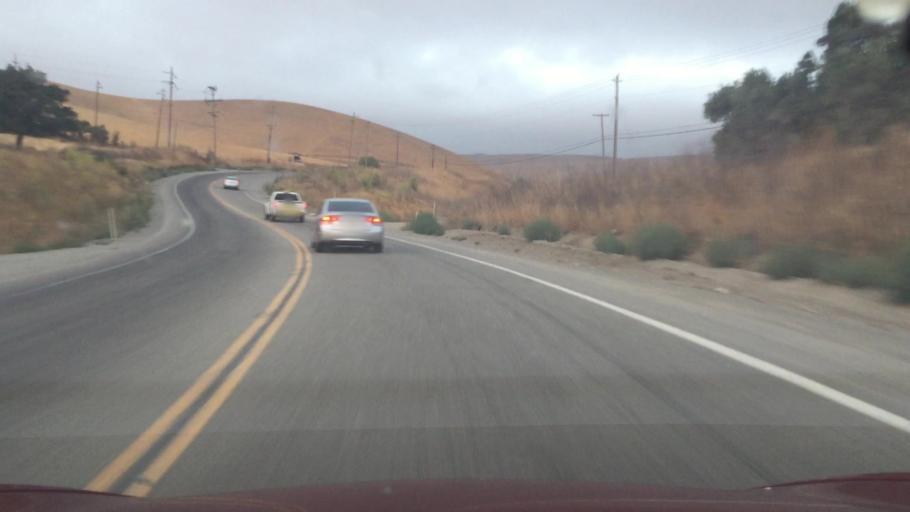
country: US
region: California
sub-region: San Joaquin County
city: Mountain House
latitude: 37.7458
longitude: -121.6597
